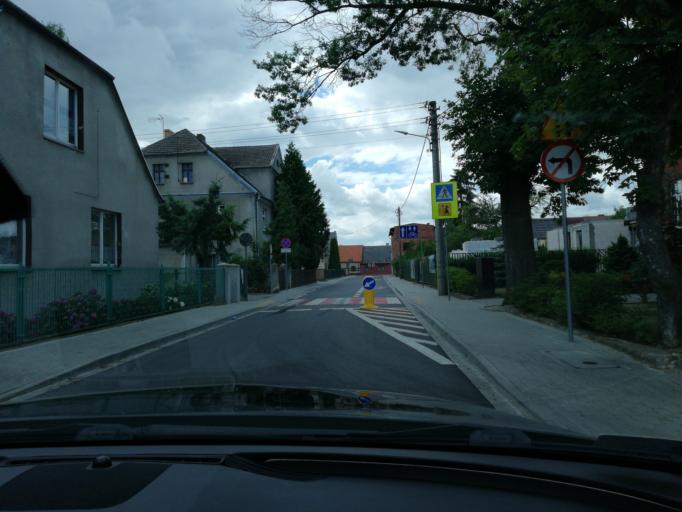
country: PL
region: Greater Poland Voivodeship
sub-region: Powiat poznanski
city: Murowana Goslina
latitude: 52.5774
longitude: 17.0124
